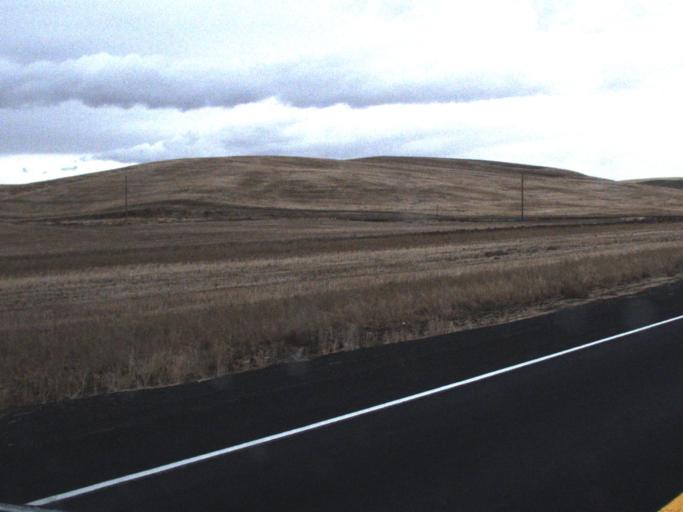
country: US
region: Washington
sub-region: Garfield County
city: Pomeroy
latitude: 46.8039
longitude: -117.7452
